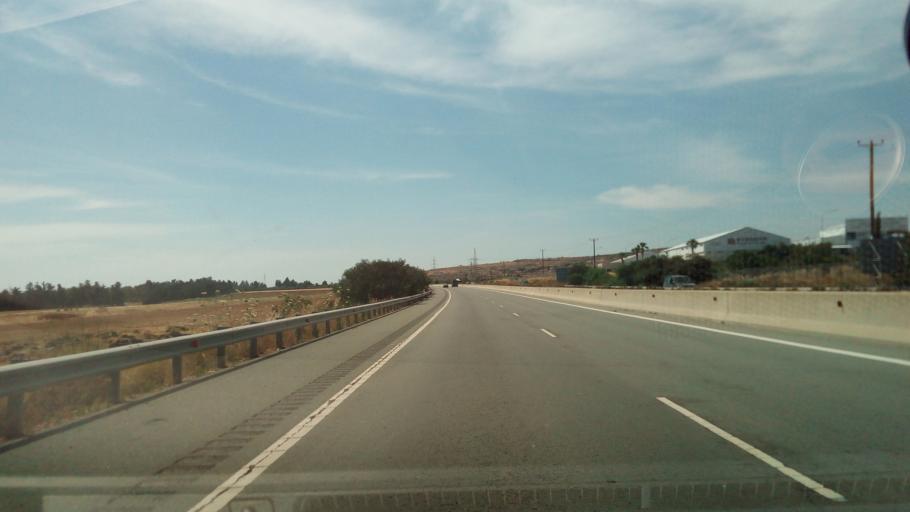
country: CY
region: Pafos
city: Mesogi
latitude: 34.7427
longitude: 32.5151
